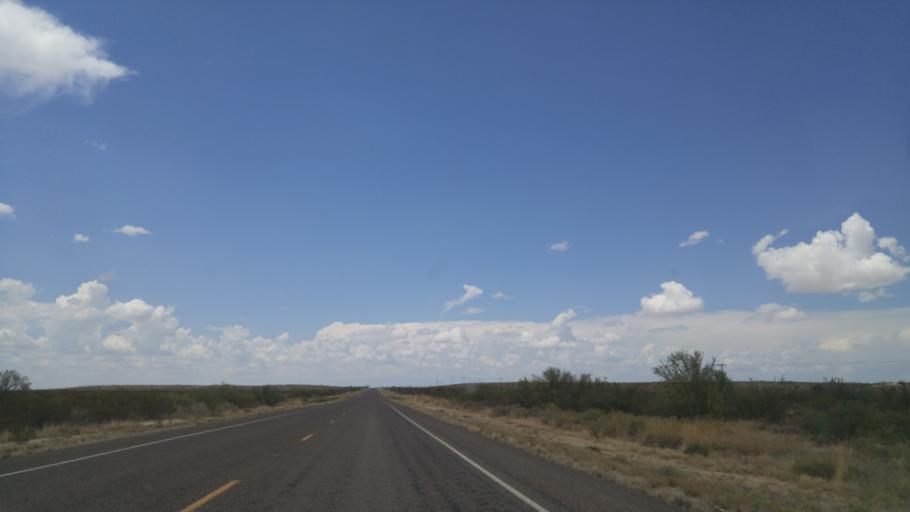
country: US
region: Texas
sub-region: Brewster County
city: Alpine
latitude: 29.6087
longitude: -103.5652
